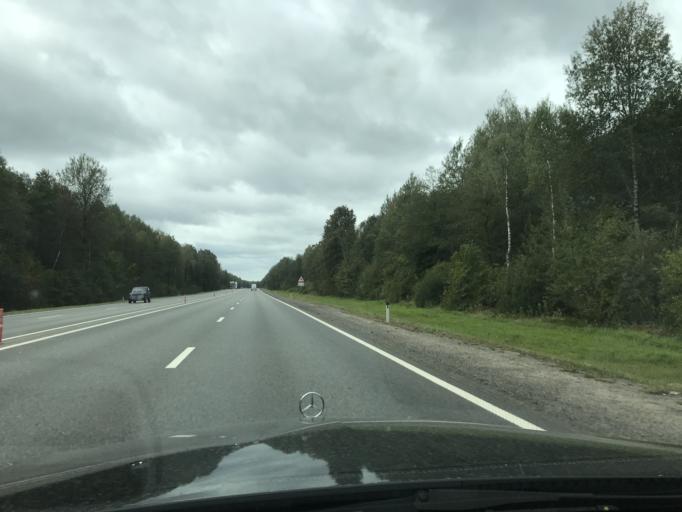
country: RU
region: Smolensk
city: Golynki
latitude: 54.7595
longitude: 31.5057
